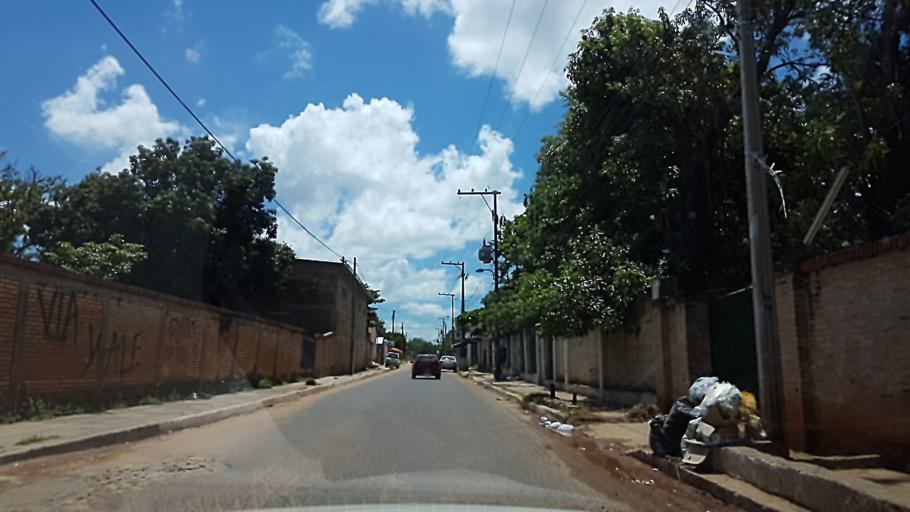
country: PY
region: Central
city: Colonia Mariano Roque Alonso
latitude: -25.2412
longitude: -57.5306
